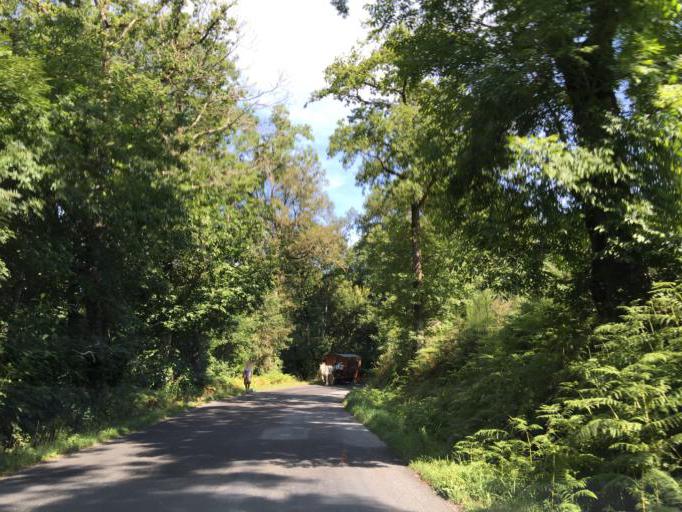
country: FR
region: Midi-Pyrenees
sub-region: Departement de l'Aveyron
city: Pont-de-Salars
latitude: 44.3095
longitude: 2.7066
